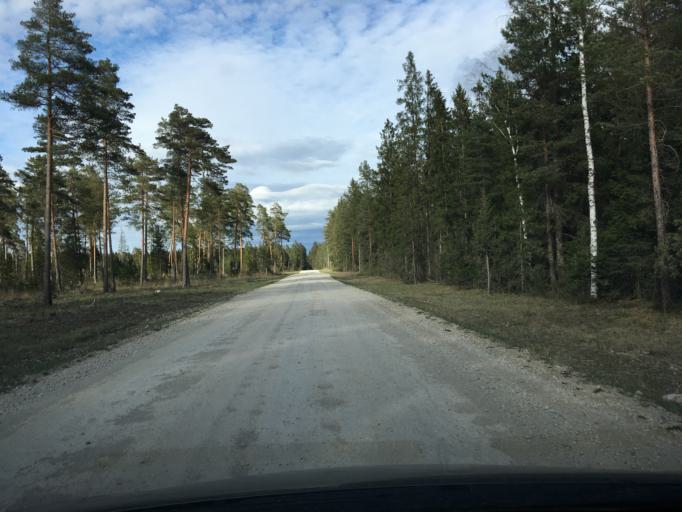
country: EE
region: Raplamaa
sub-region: Maerjamaa vald
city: Marjamaa
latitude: 59.0159
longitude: 24.4191
